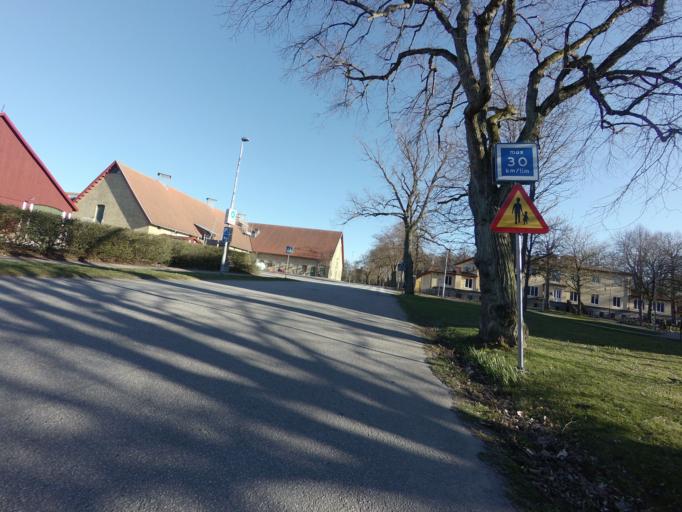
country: SE
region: Skane
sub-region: Lomma Kommun
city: Lomma
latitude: 55.6574
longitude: 13.0826
